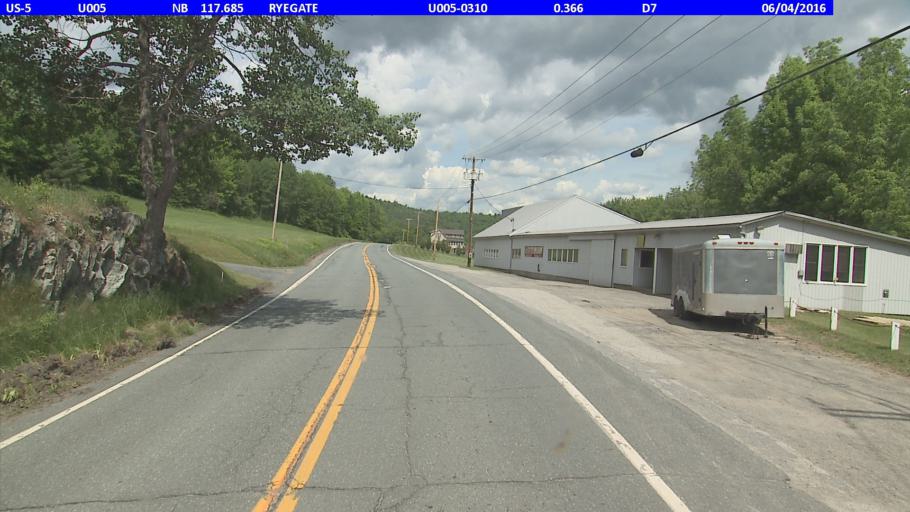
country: US
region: New Hampshire
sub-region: Grafton County
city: Woodsville
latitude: 44.1628
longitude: -72.0493
